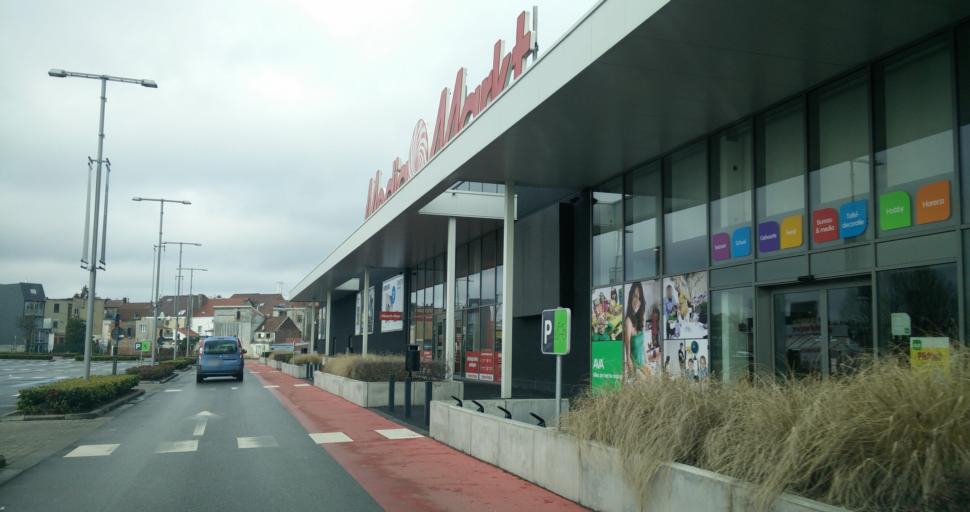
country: BE
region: Flanders
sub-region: Provincie Vlaams-Brabant
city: Drogenbos
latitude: 50.8054
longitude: 4.2915
